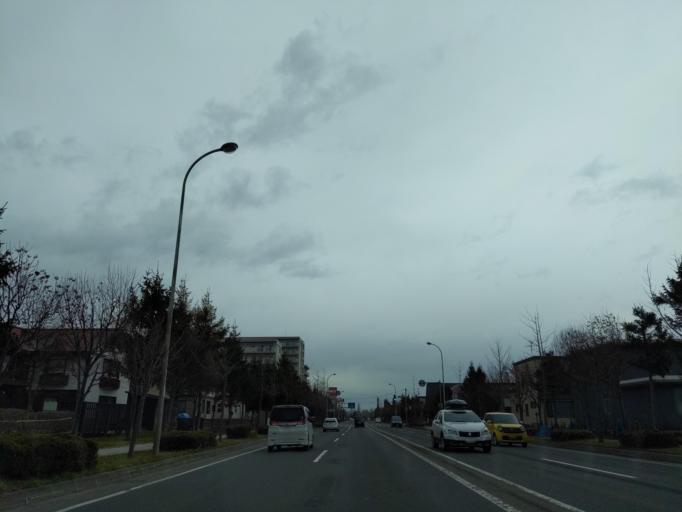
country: JP
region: Hokkaido
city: Sapporo
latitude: 43.1396
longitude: 141.3700
